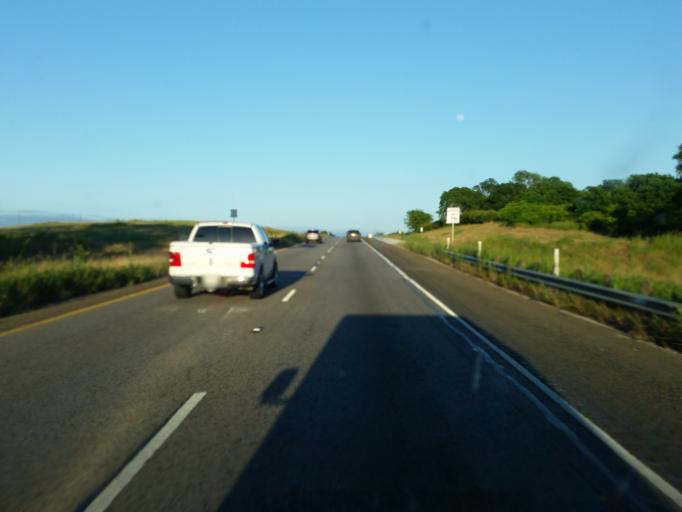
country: US
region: Texas
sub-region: Van Zandt County
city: Wills Point
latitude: 32.6651
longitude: -96.1331
